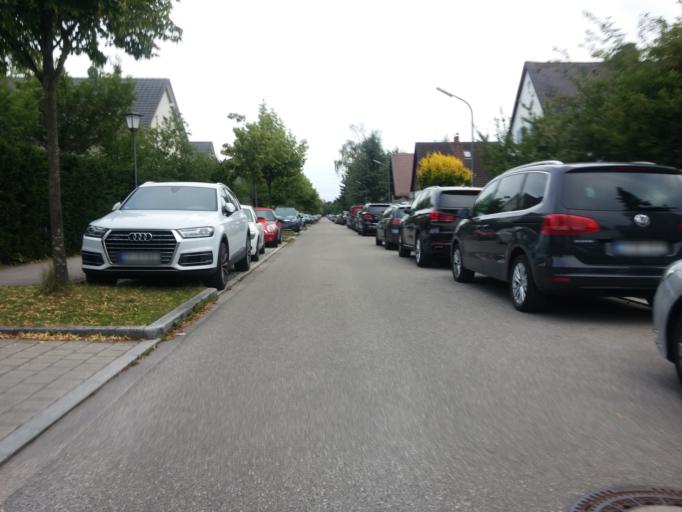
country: DE
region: Bavaria
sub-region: Upper Bavaria
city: Neubiberg
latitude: 48.1193
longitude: 11.6646
